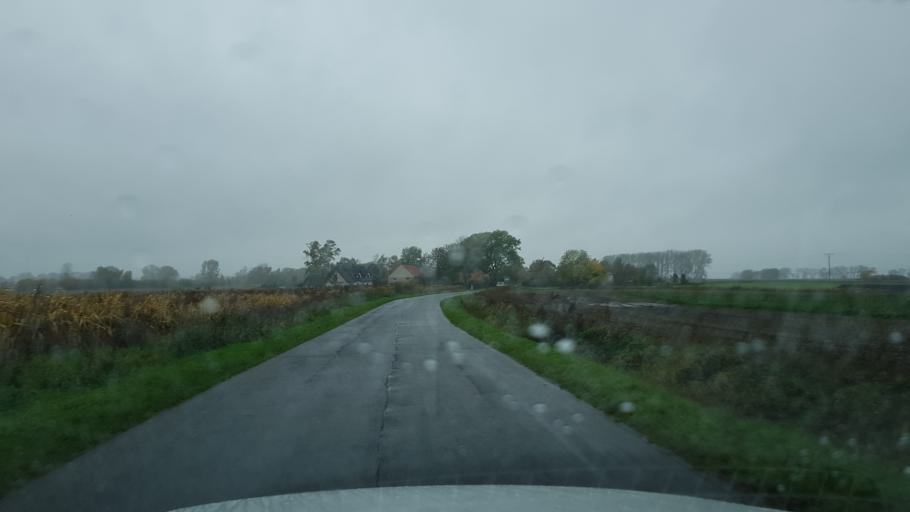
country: PL
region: West Pomeranian Voivodeship
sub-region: Powiat pyrzycki
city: Pyrzyce
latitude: 53.1585
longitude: 14.8522
